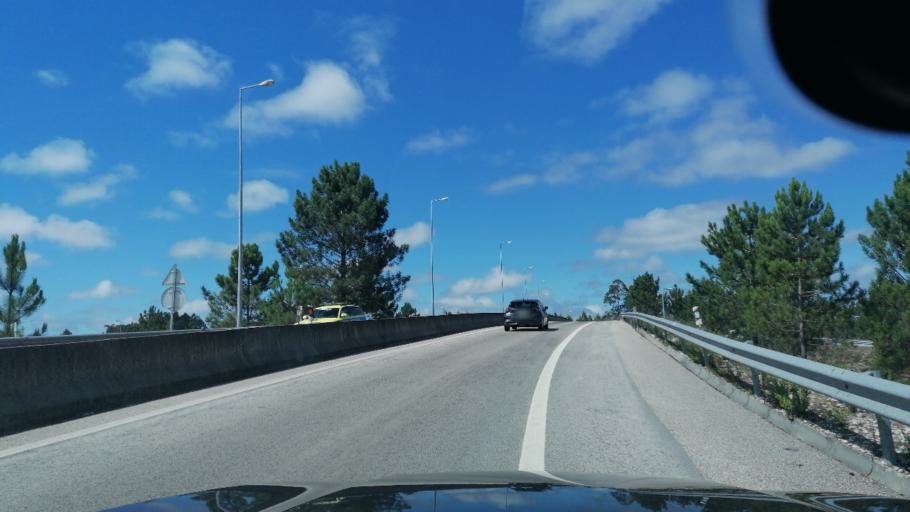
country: PT
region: Leiria
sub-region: Leiria
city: Maceira
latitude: 39.7421
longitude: -8.8713
